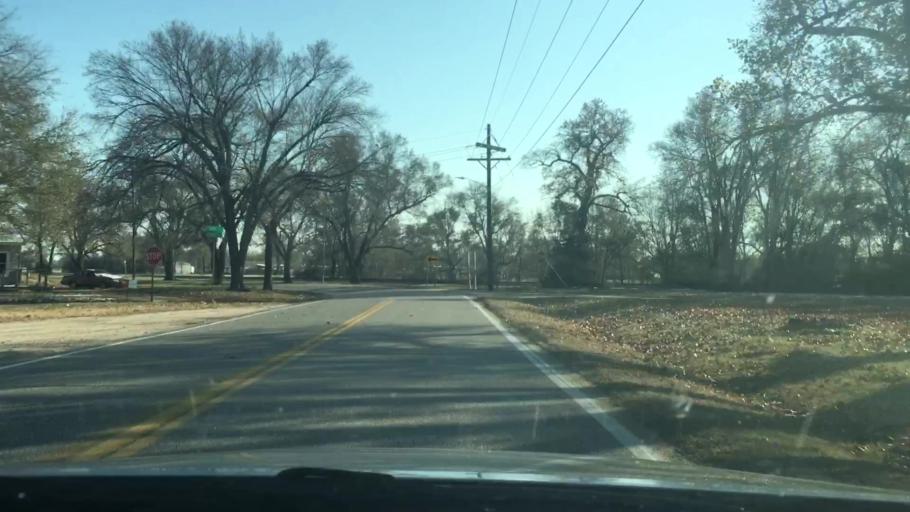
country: US
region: Kansas
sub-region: Reno County
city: Nickerson
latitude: 38.1504
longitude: -98.0873
